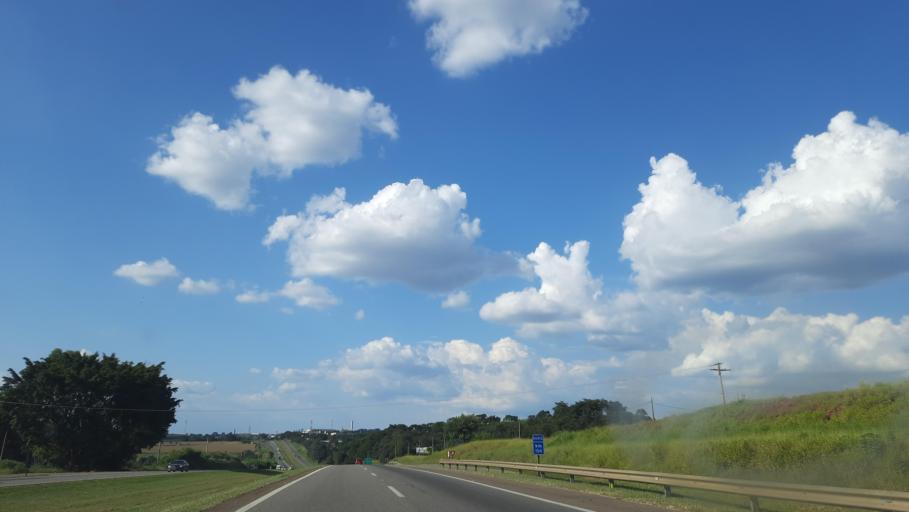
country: BR
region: Sao Paulo
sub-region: Mogi-Mirim
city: Mogi Mirim
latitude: -22.5049
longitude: -46.9862
